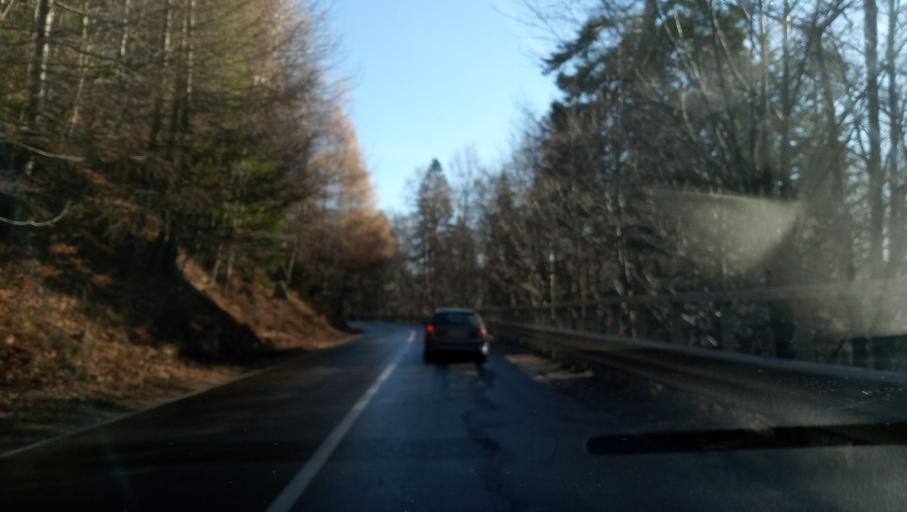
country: RO
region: Brasov
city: Crivina
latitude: 45.4702
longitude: 25.9243
